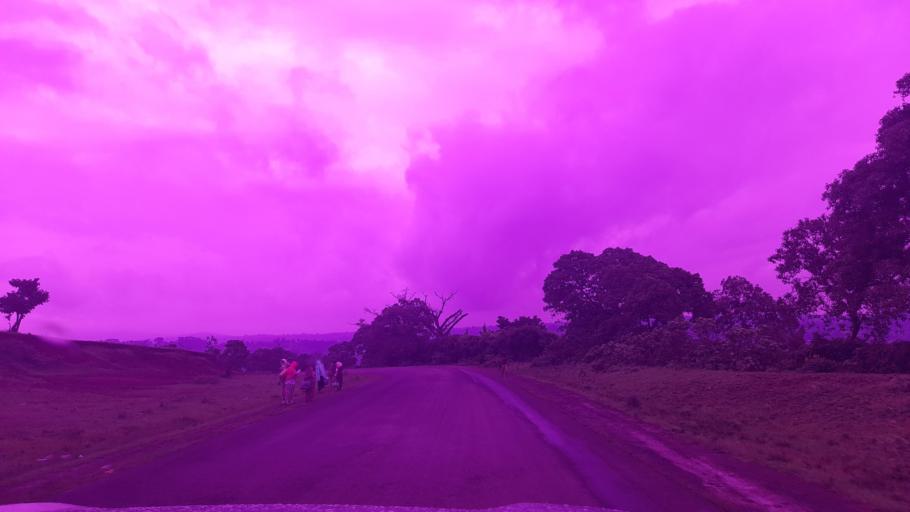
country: ET
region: Oromiya
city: Jima
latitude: 7.6924
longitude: 37.2438
